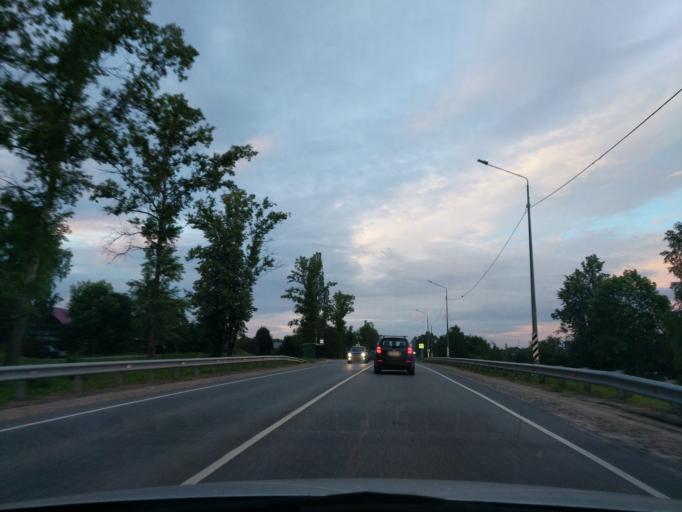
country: RU
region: Kaluga
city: Obninsk
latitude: 55.0741
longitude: 36.6191
